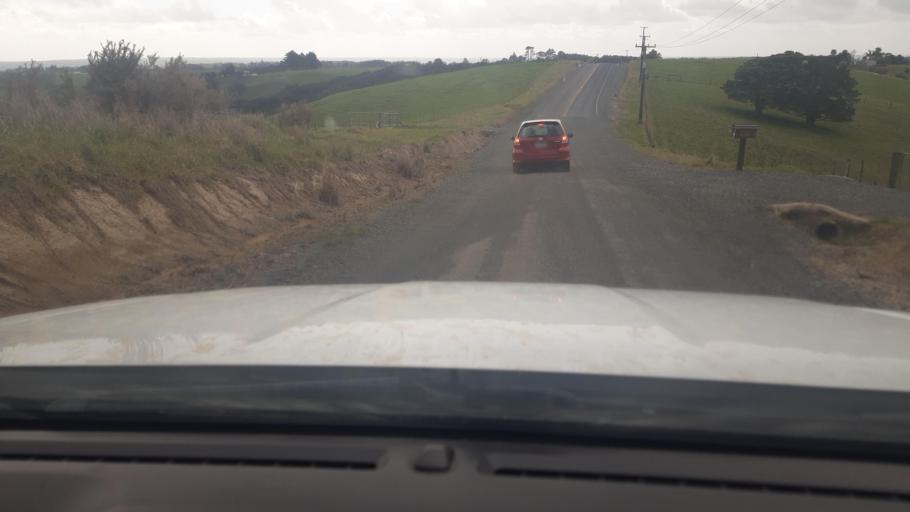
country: NZ
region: Northland
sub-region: Far North District
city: Kaitaia
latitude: -35.0546
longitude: 173.3256
